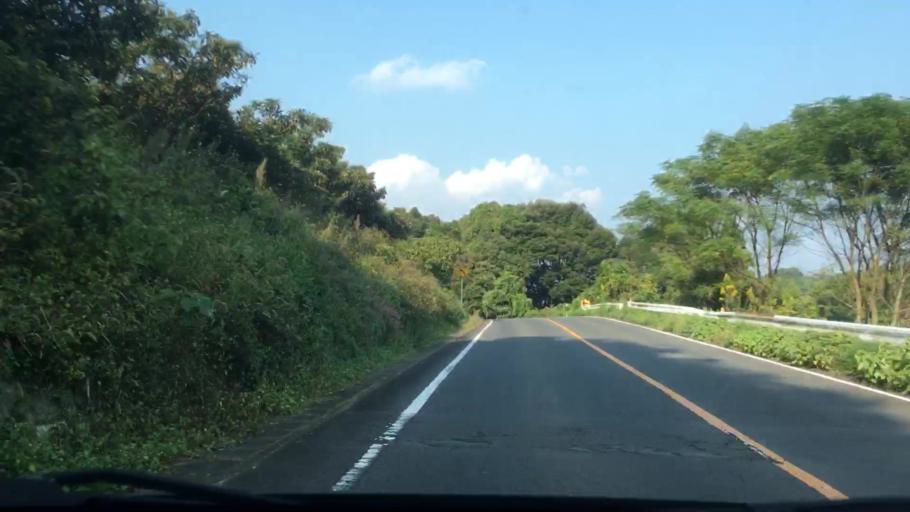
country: JP
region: Nagasaki
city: Sasebo
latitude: 33.0390
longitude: 129.6868
